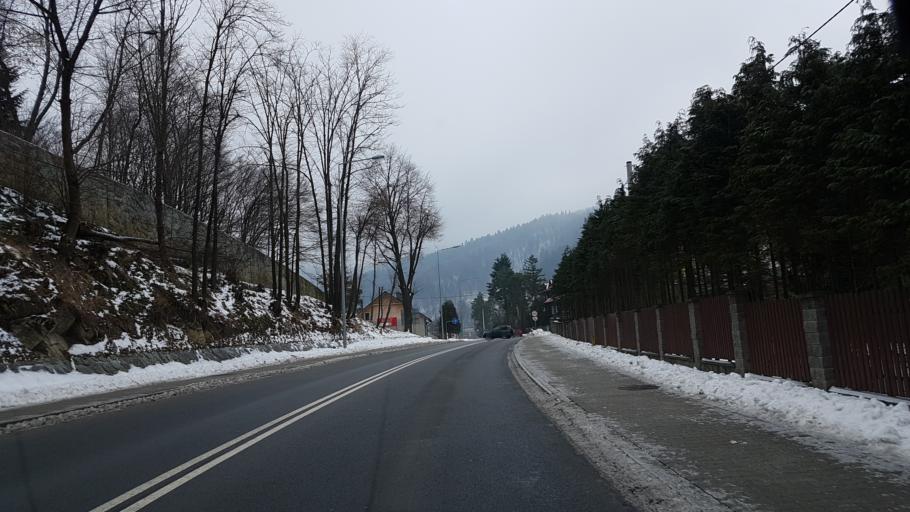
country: PL
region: Lesser Poland Voivodeship
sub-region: Powiat nowosadecki
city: Piwniczna-Zdroj
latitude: 49.4224
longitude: 20.7255
